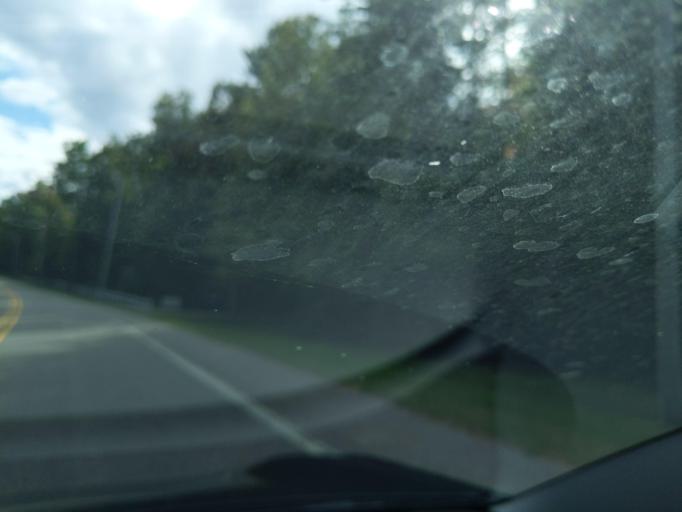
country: US
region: Michigan
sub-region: Antrim County
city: Bellaire
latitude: 44.9337
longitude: -85.2874
